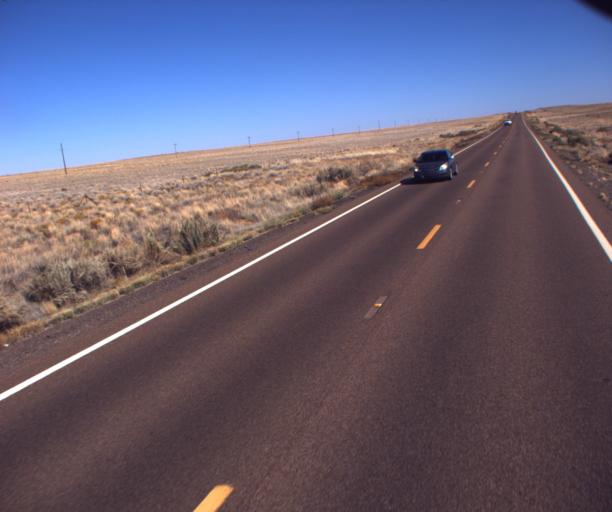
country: US
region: Arizona
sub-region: Navajo County
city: Winslow
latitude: 35.0772
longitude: -110.5637
